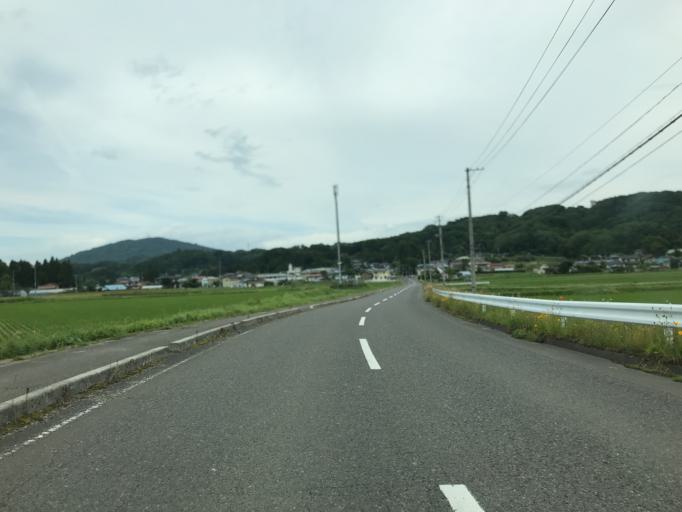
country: JP
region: Fukushima
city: Funehikimachi-funehiki
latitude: 37.3947
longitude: 140.5651
